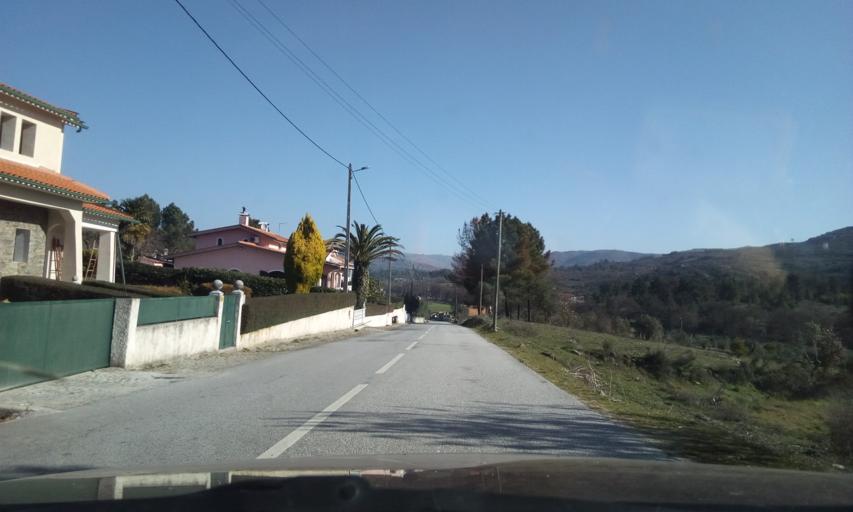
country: PT
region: Guarda
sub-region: Fornos de Algodres
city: Fornos de Algodres
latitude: 40.6488
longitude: -7.4677
